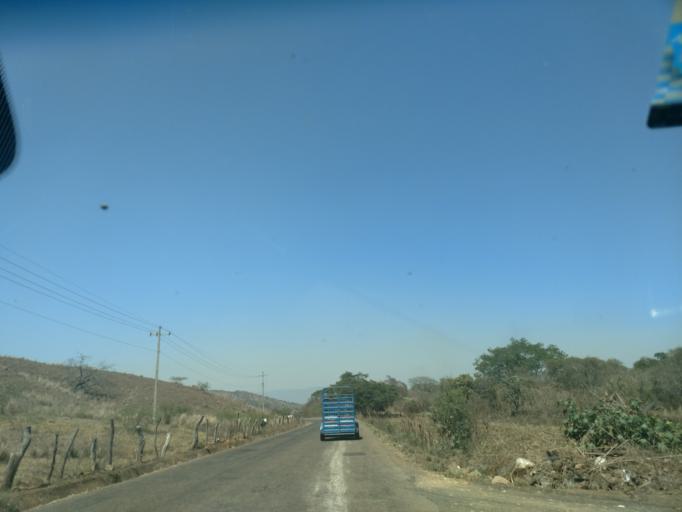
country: MX
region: Nayarit
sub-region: Tepic
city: La Corregidora
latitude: 21.5020
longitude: -104.7339
